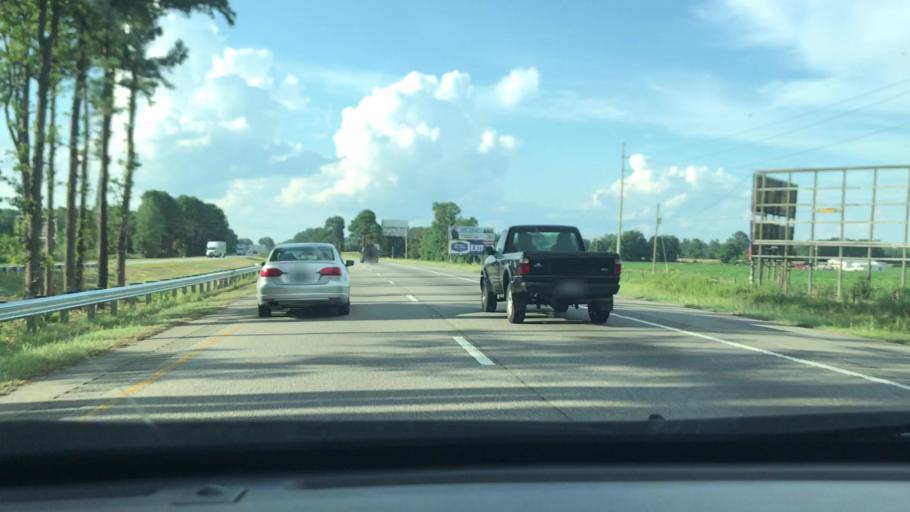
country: US
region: North Carolina
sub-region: Robeson County
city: Lumberton
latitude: 34.6920
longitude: -78.9987
